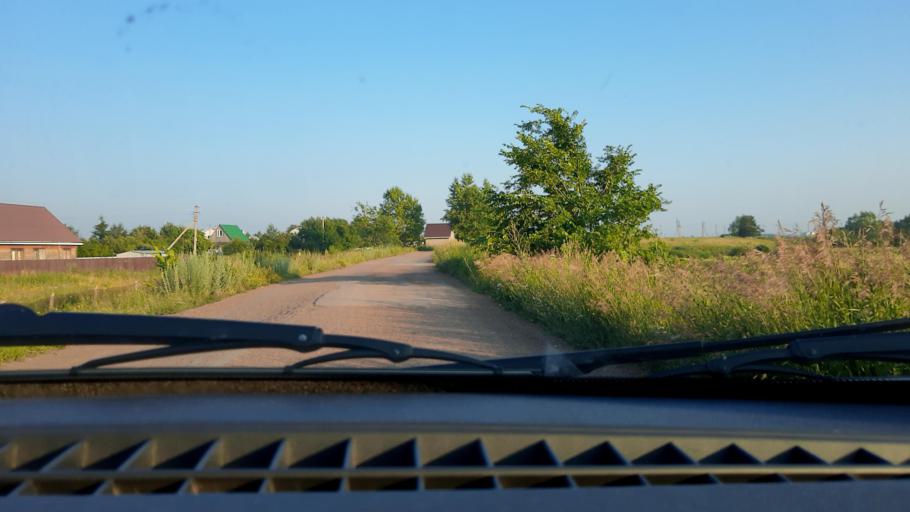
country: RU
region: Bashkortostan
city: Asanovo
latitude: 54.9170
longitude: 55.6266
